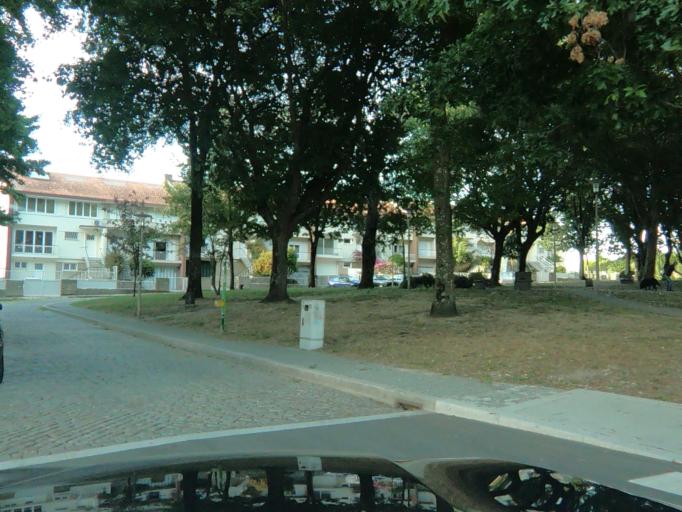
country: PT
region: Porto
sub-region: Matosinhos
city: Sao Mamede de Infesta
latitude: 41.1787
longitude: -8.6185
